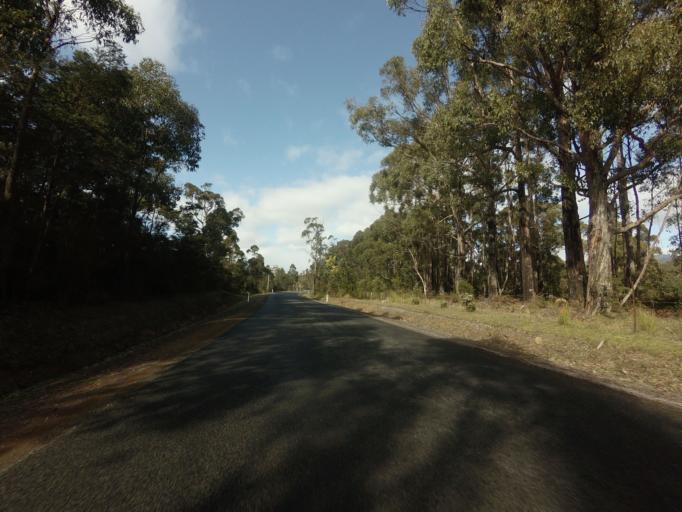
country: AU
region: Tasmania
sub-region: Huon Valley
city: Geeveston
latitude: -43.4190
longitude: 146.9078
